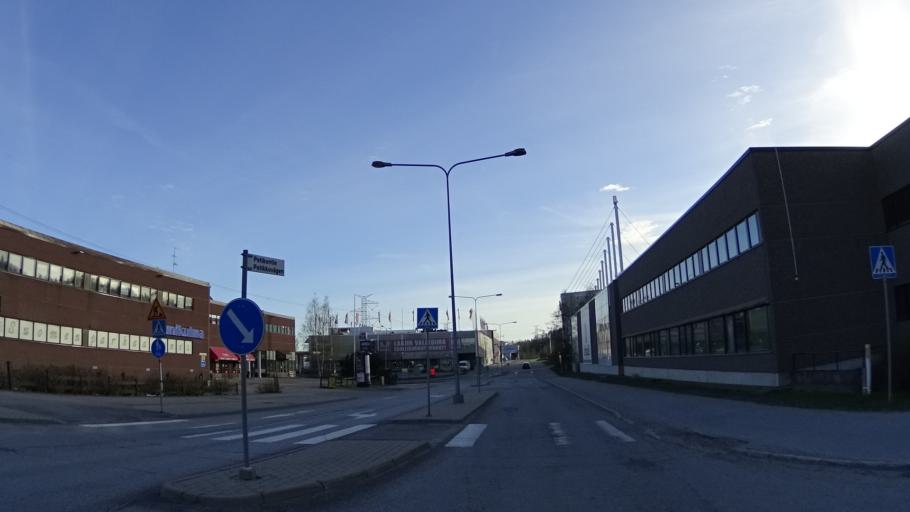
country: FI
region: Uusimaa
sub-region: Helsinki
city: Kilo
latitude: 60.2784
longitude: 24.8128
